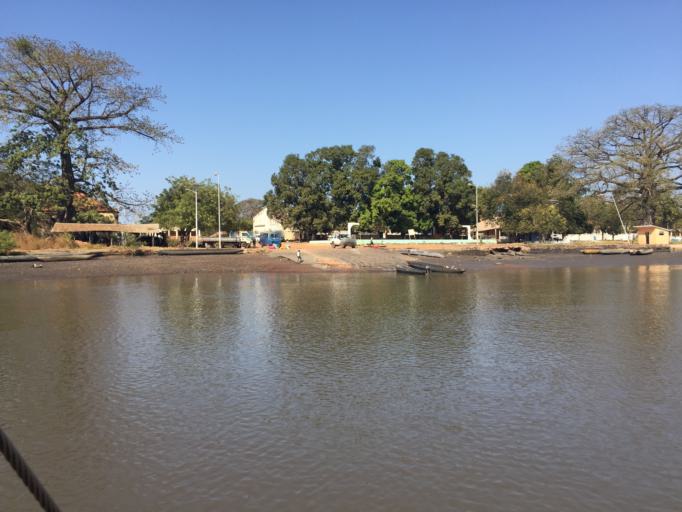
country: GW
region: Oio
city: Farim
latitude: 12.4789
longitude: -15.2223
